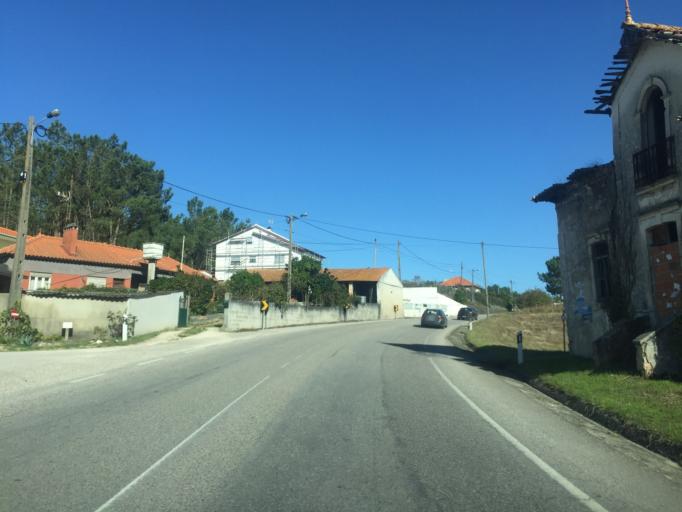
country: PT
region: Leiria
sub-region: Leiria
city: Monte Redondo
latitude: 39.9097
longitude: -8.8215
